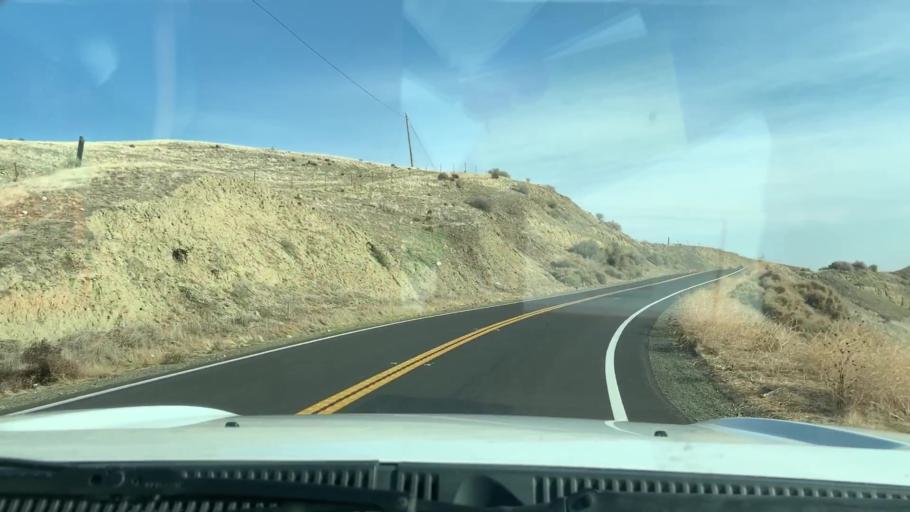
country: US
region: California
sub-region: Fresno County
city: Coalinga
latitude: 36.1136
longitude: -120.3875
